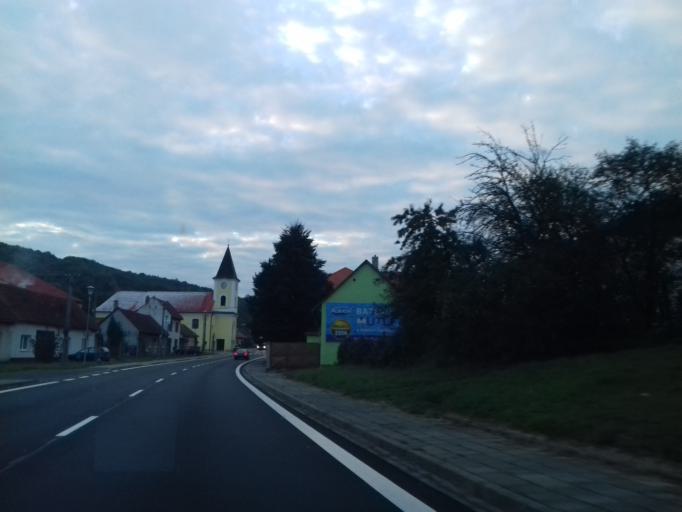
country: CZ
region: Zlin
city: Bojkovice
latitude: 48.9649
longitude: 17.8669
